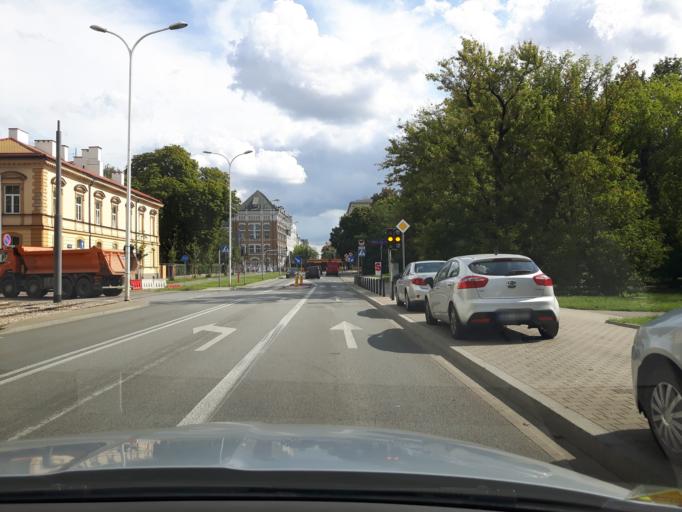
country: PL
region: Masovian Voivodeship
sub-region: Warszawa
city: Praga Polnoc
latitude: 52.2549
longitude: 21.0311
